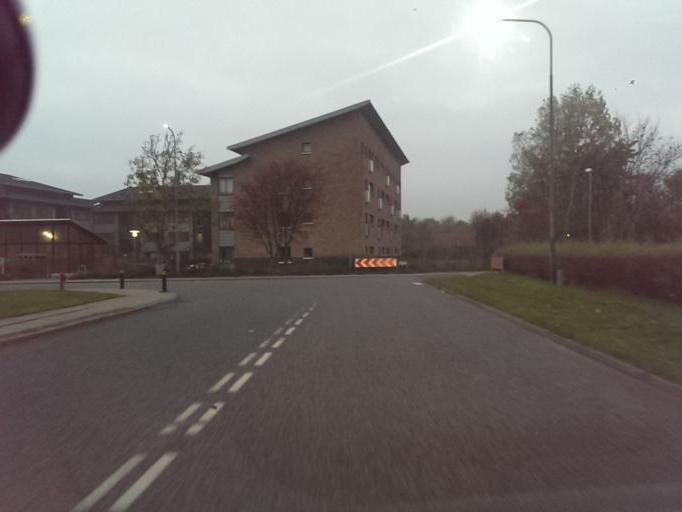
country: DK
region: South Denmark
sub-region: Esbjerg Kommune
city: Esbjerg
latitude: 55.5071
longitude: 8.4458
